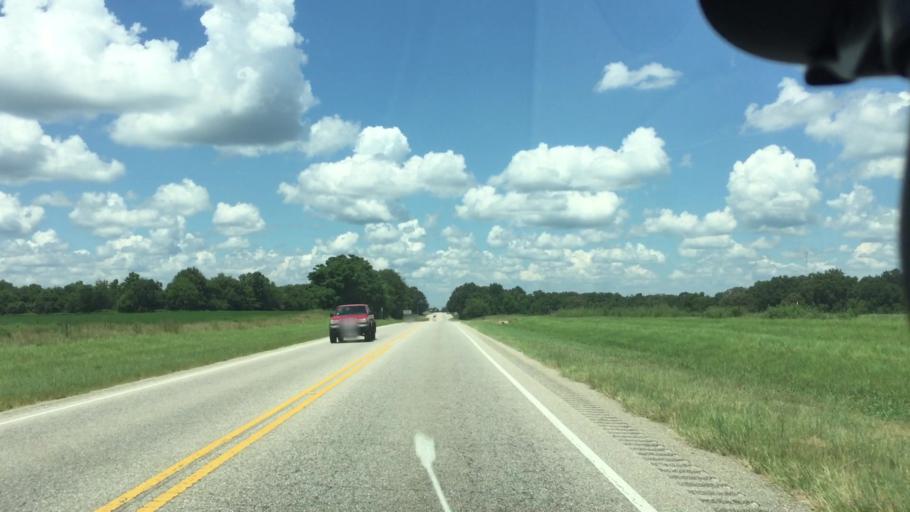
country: US
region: Alabama
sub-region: Coffee County
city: New Brockton
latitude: 31.4200
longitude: -85.8863
